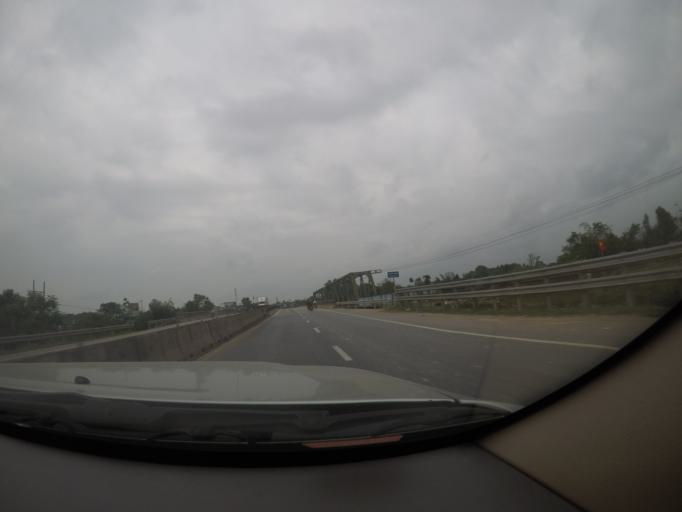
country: VN
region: Quang Tri
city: Hai Lang
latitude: 16.6334
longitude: 107.3020
